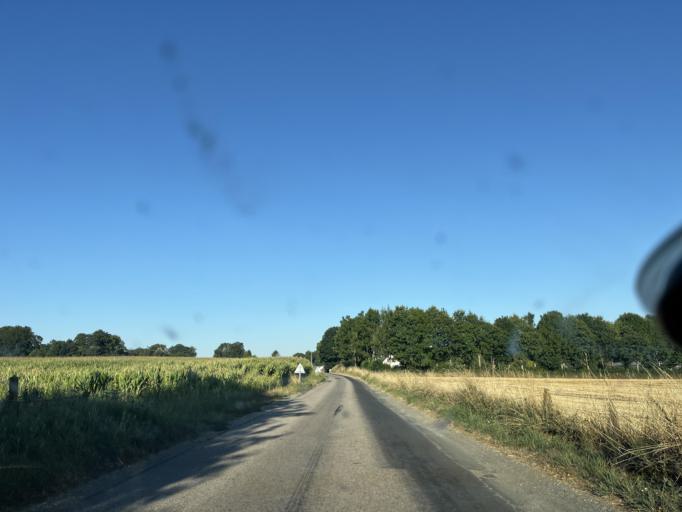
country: FR
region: Haute-Normandie
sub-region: Departement de la Seine-Maritime
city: Fauville-en-Caux
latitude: 49.6221
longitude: 0.6215
